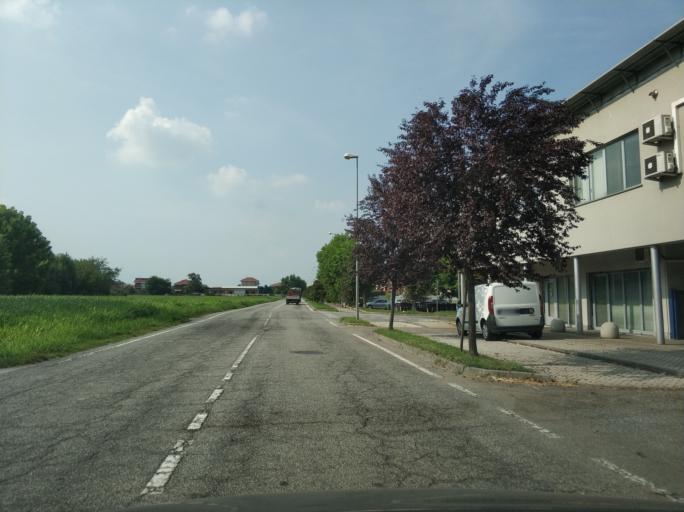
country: IT
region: Piedmont
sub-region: Provincia di Torino
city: Leini
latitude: 45.1774
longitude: 7.7096
